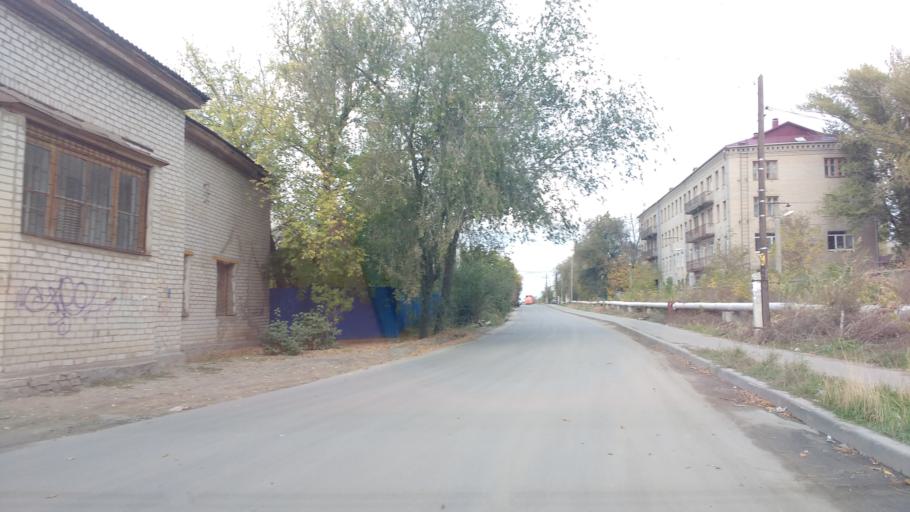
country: RU
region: Volgograd
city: Vodstroy
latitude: 48.7754
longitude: 44.5413
